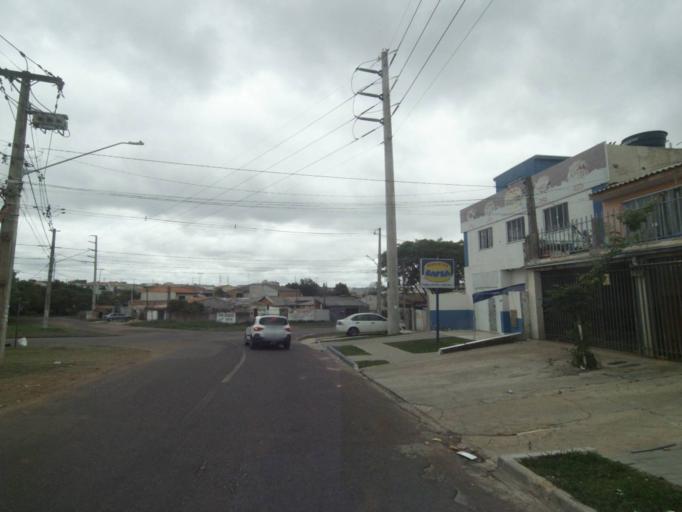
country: BR
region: Parana
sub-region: Sao Jose Dos Pinhais
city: Sao Jose dos Pinhais
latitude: -25.5530
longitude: -49.2564
